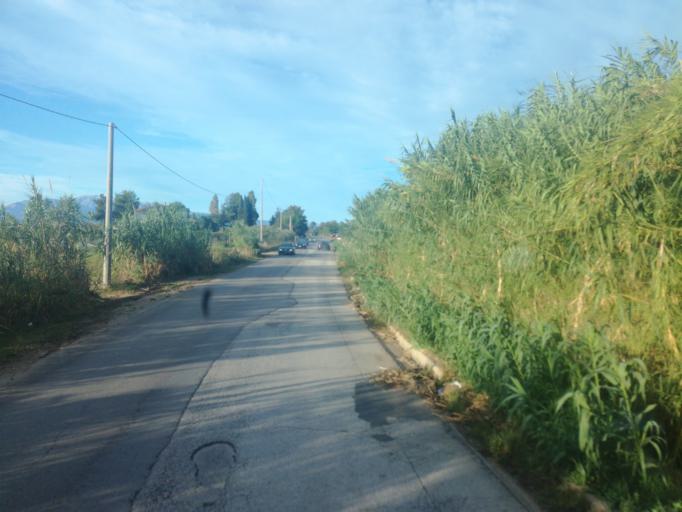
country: IT
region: Abruzzo
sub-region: Provincia di Chieti
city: Miglianico
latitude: 42.3853
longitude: 14.2939
